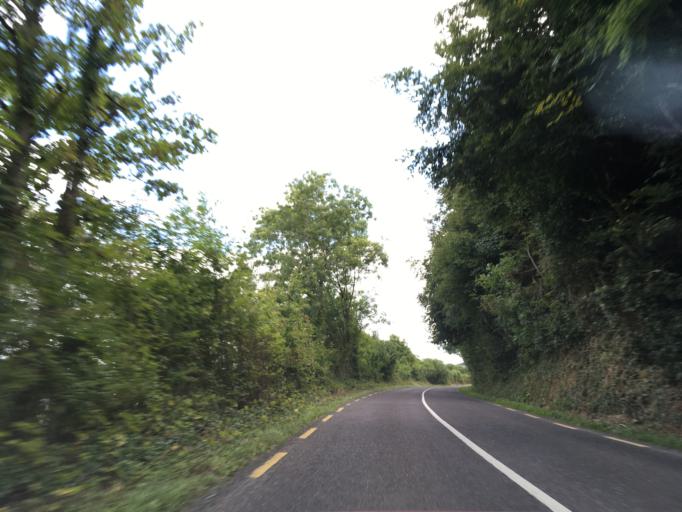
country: IE
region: Munster
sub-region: County Cork
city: Carrigaline
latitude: 51.8100
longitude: -8.3545
